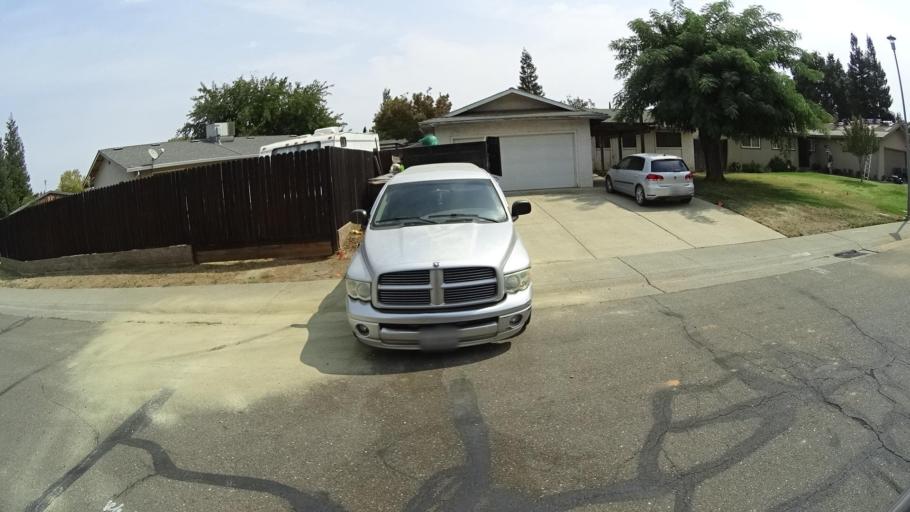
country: US
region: California
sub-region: Sacramento County
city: Elk Grove
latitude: 38.4175
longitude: -121.3797
